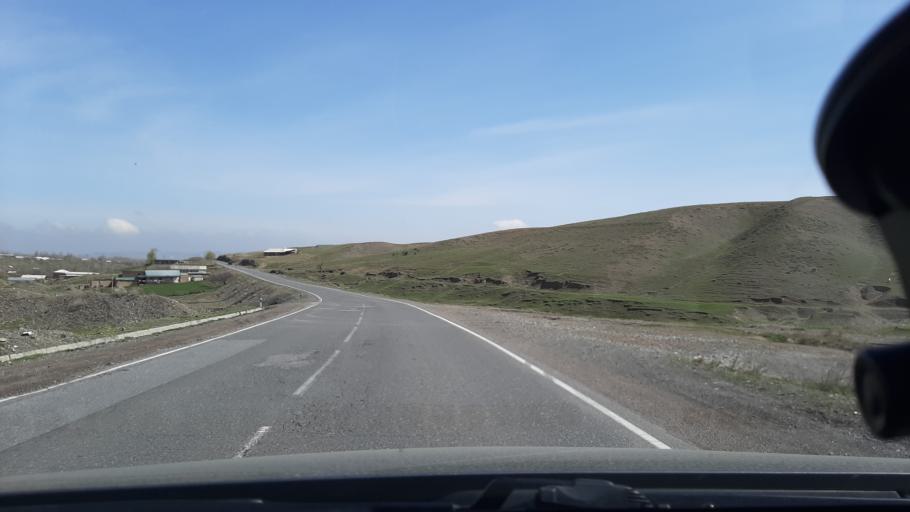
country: TJ
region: Viloyati Sughd
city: Shahriston
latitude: 39.7634
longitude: 68.8164
